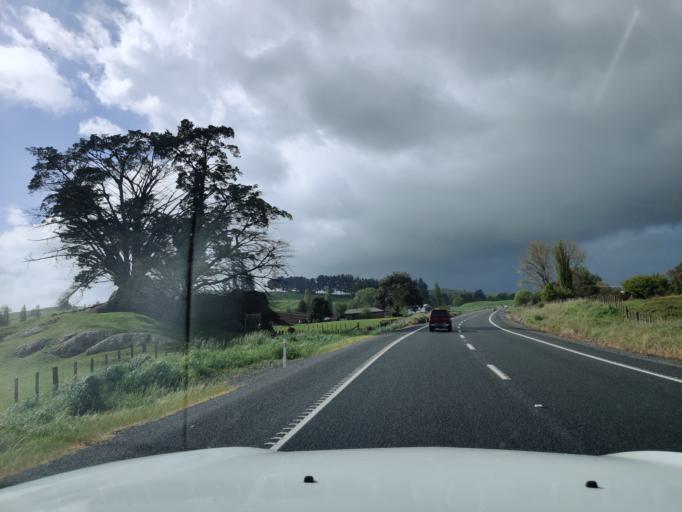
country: NZ
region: Waikato
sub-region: Matamata-Piako District
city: Matamata
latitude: -37.9559
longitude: 175.6839
